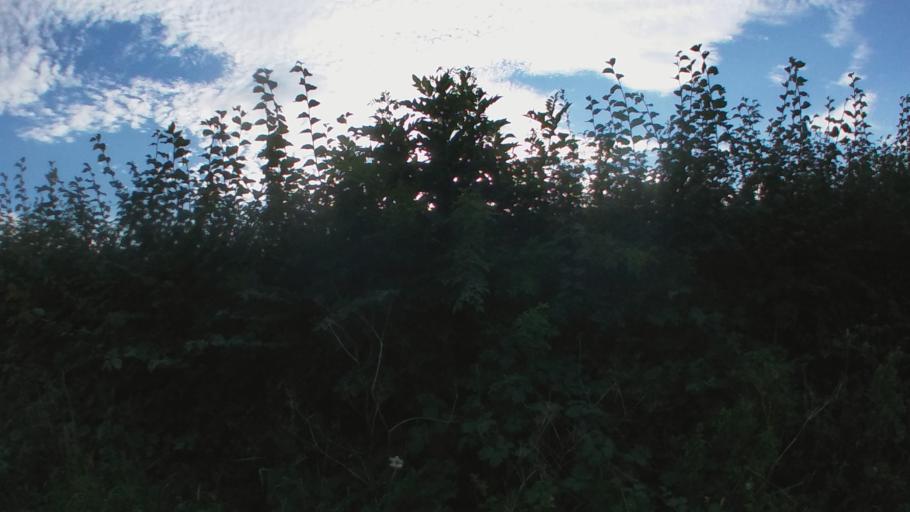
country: IE
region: Leinster
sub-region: Kilkenny
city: Kilkenny
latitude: 52.6871
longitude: -7.2191
